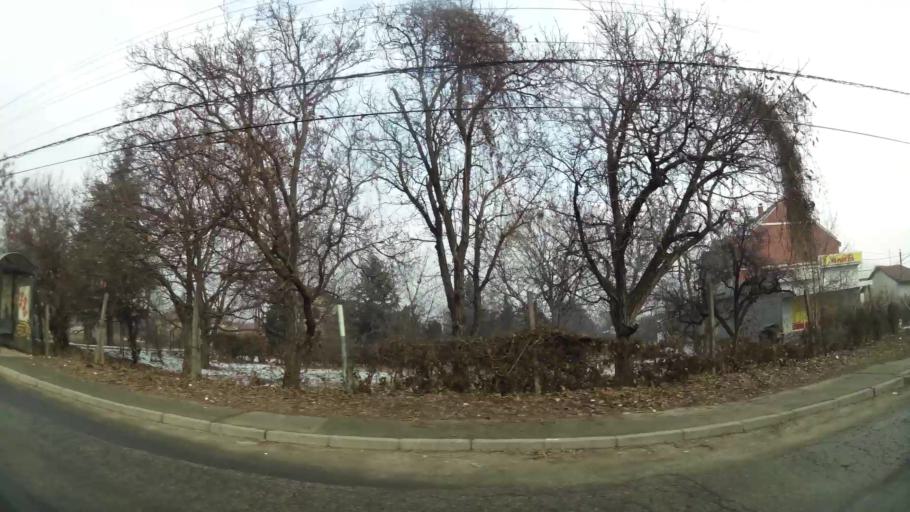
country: MK
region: Kisela Voda
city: Kisela Voda
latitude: 41.9946
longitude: 21.5040
